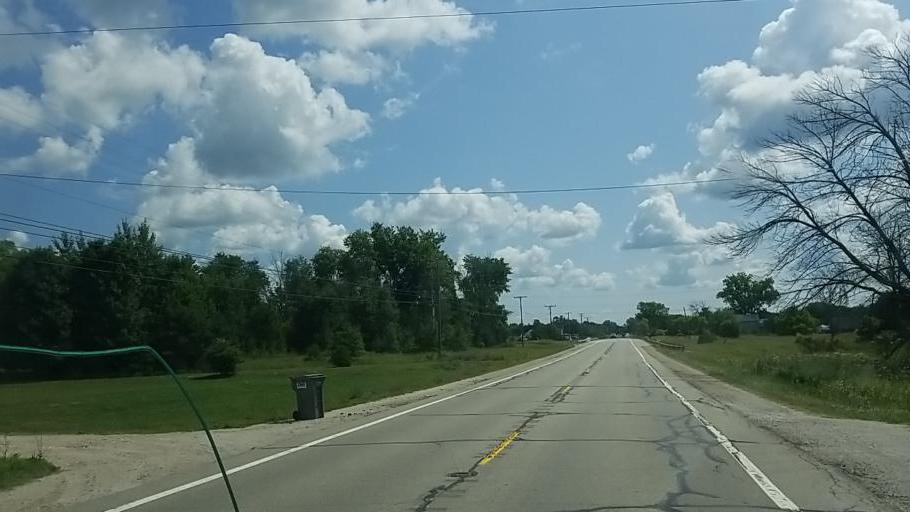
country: US
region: Michigan
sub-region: Muskegon County
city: Ravenna
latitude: 43.2351
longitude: -85.9780
